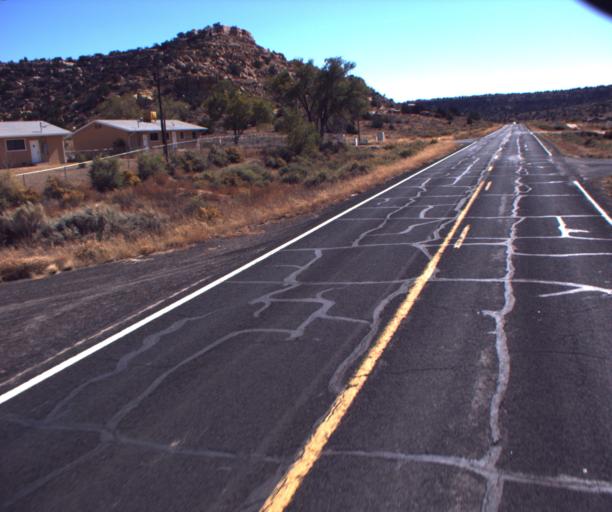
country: US
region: Arizona
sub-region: Navajo County
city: First Mesa
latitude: 35.8235
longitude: -110.2196
